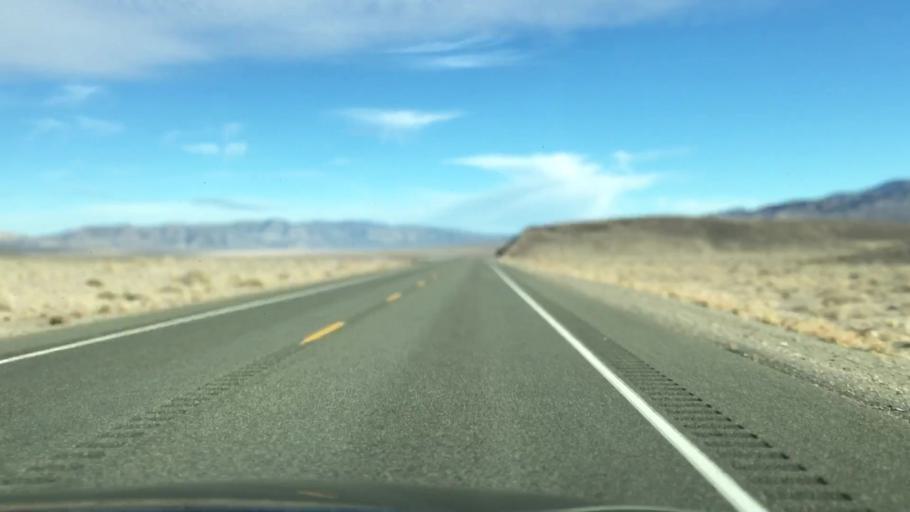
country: US
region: Nevada
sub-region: Mineral County
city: Hawthorne
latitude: 38.5461
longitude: -118.4137
